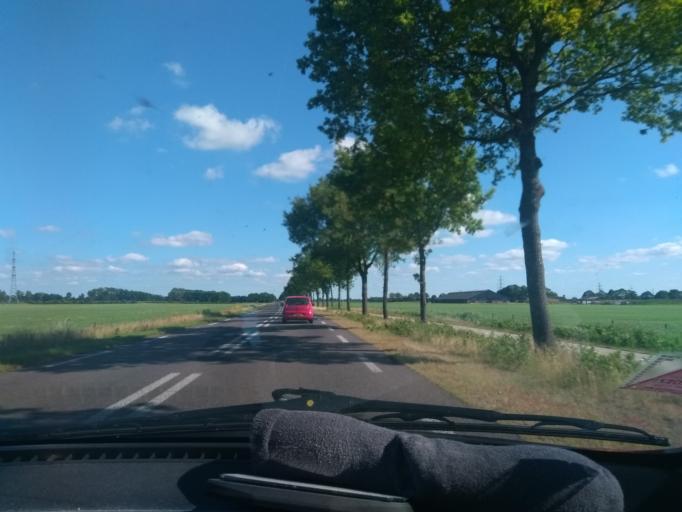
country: NL
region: Drenthe
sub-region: Gemeente Tynaarlo
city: Vries
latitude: 53.1222
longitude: 6.5052
